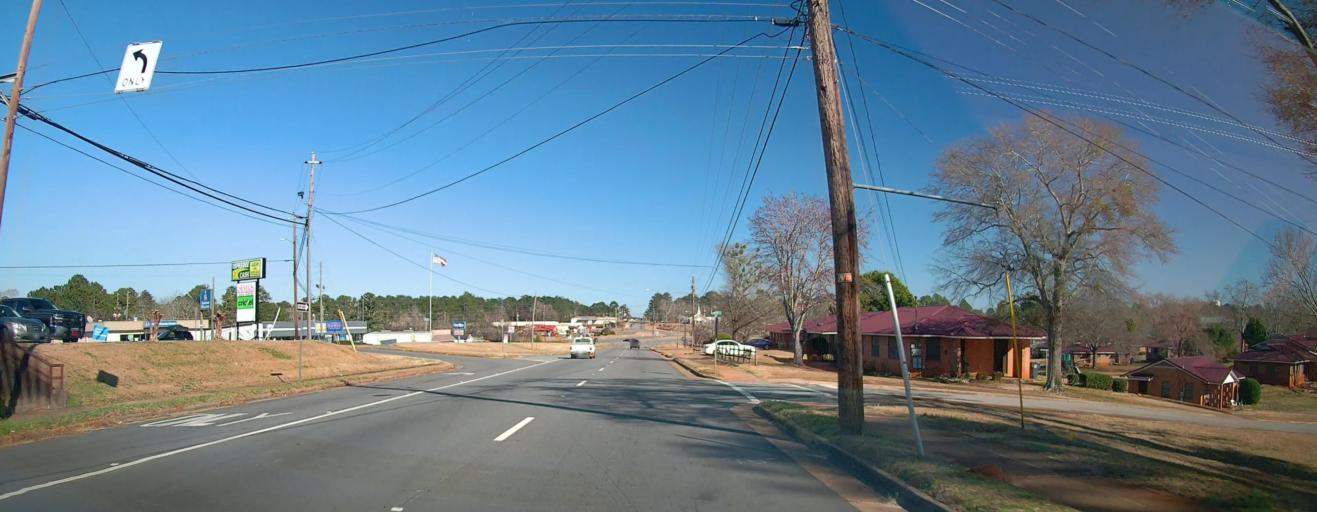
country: US
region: Georgia
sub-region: Sumter County
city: Americus
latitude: 32.0712
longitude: -84.2130
